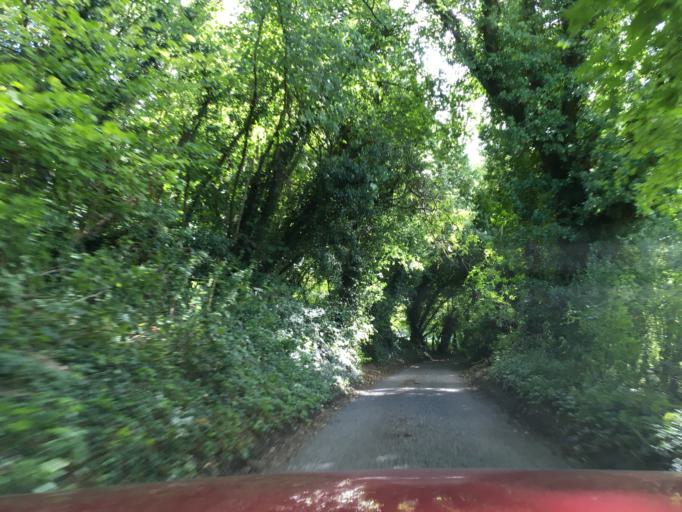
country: GB
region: England
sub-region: Hampshire
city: Winchester
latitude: 51.0817
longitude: -1.3751
